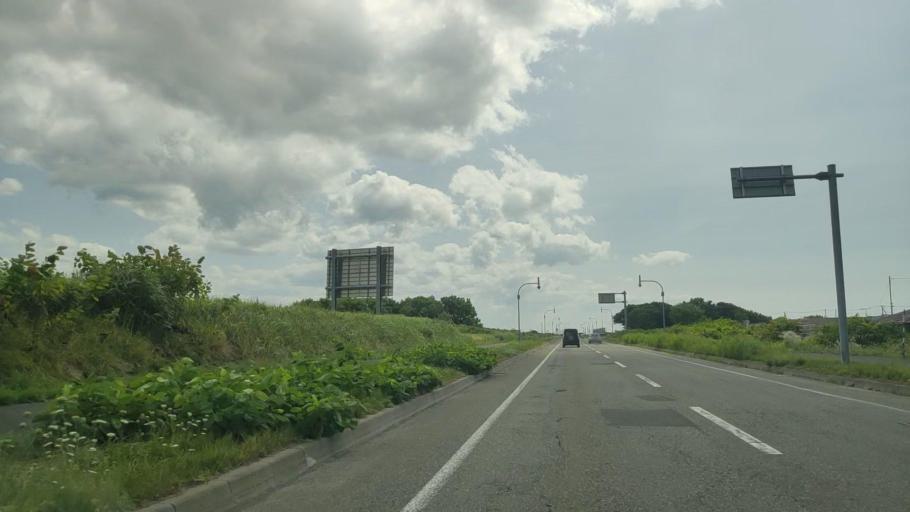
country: JP
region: Hokkaido
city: Makubetsu
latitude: 44.8764
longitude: 141.7508
